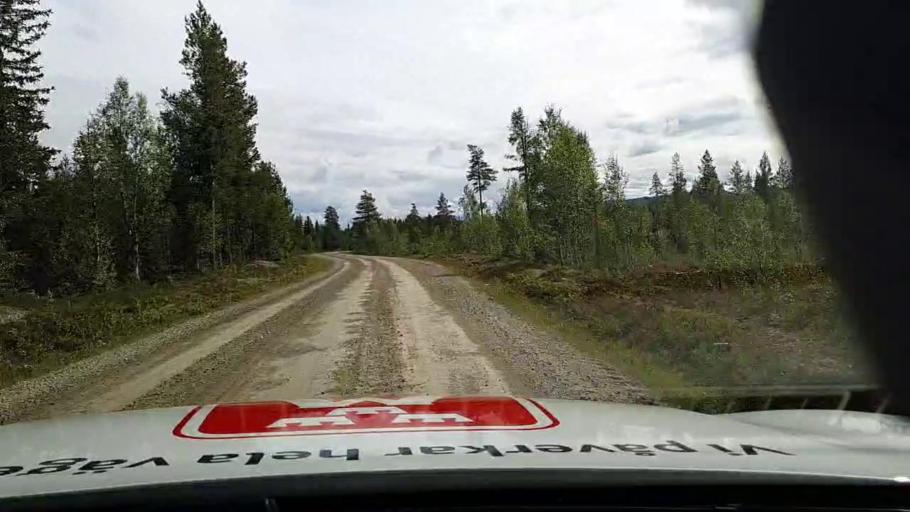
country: SE
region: Jaemtland
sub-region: Are Kommun
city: Jarpen
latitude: 62.5265
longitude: 13.4875
